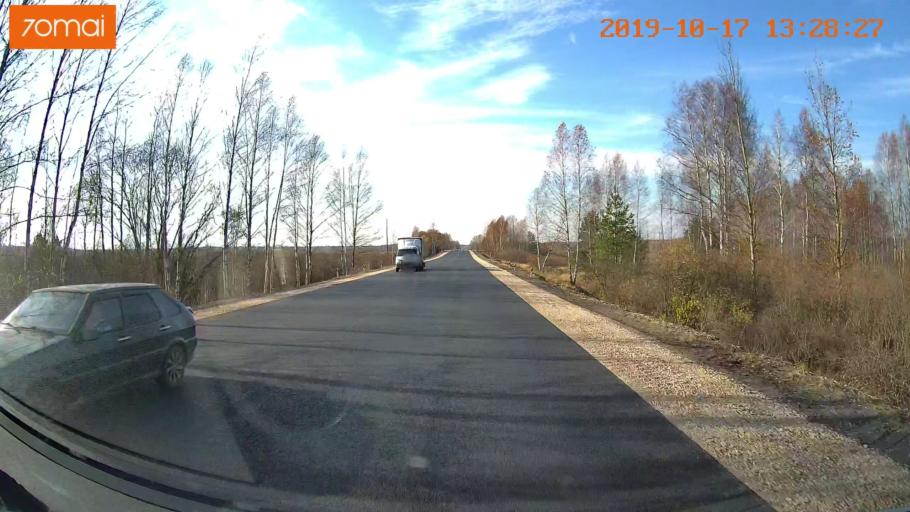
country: RU
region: Vladimir
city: Velikodvorskiy
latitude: 55.1162
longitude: 40.8681
